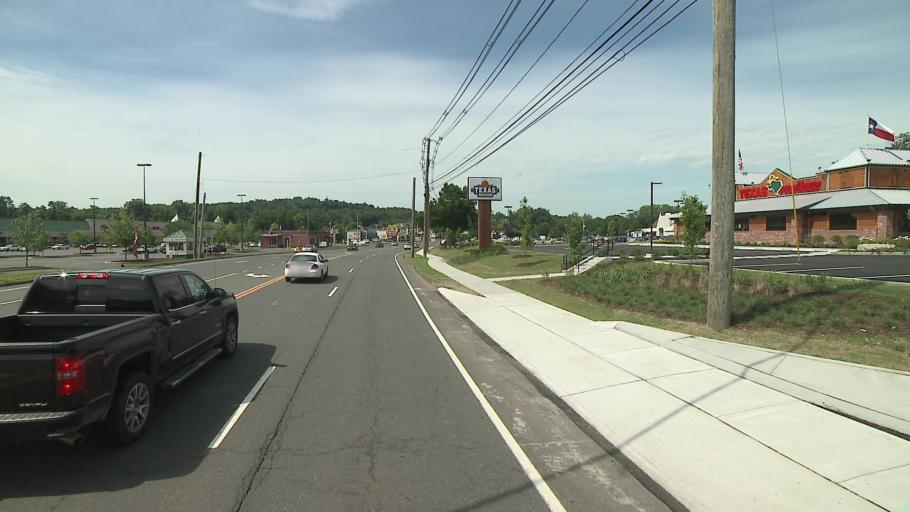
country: US
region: Connecticut
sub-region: Fairfield County
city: Bethel
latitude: 41.4079
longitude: -73.4163
